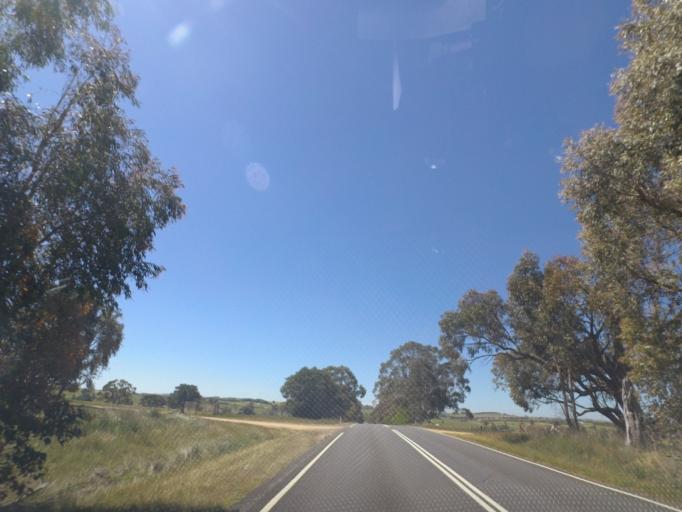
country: AU
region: Victoria
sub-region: Hume
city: Sunbury
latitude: -37.1580
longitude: 144.7666
